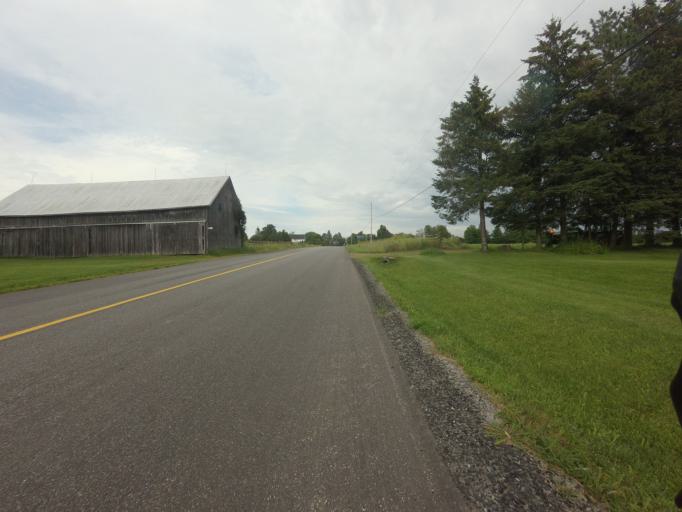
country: CA
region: Ontario
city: Perth
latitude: 45.0937
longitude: -76.3952
